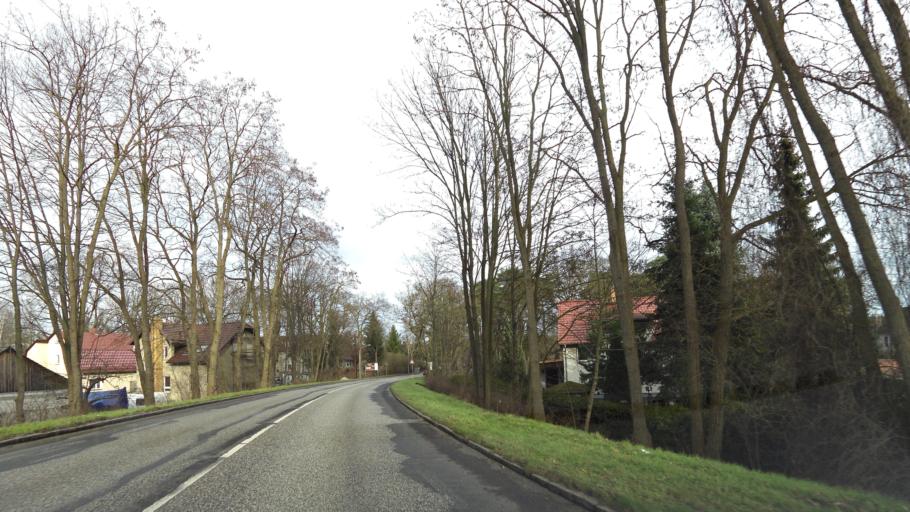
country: DE
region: Brandenburg
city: Petershagen
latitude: 52.5329
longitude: 13.8186
